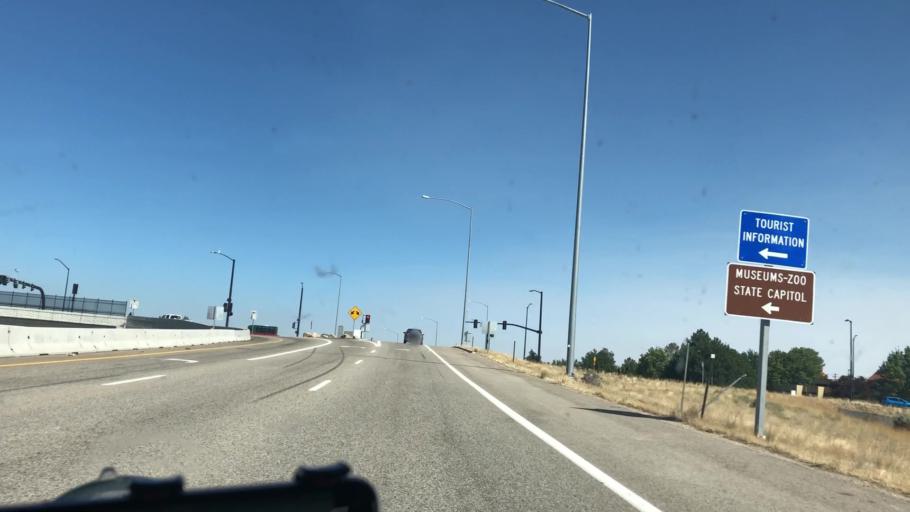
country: US
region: Idaho
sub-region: Ada County
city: Boise
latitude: 43.5712
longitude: -116.2173
